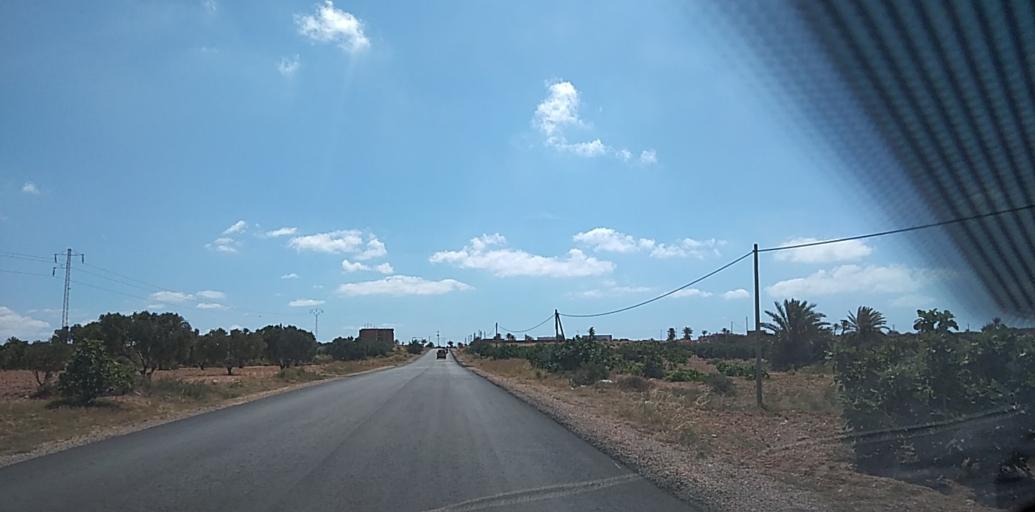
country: TN
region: Safaqis
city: Al Qarmadah
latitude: 34.6574
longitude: 11.0772
